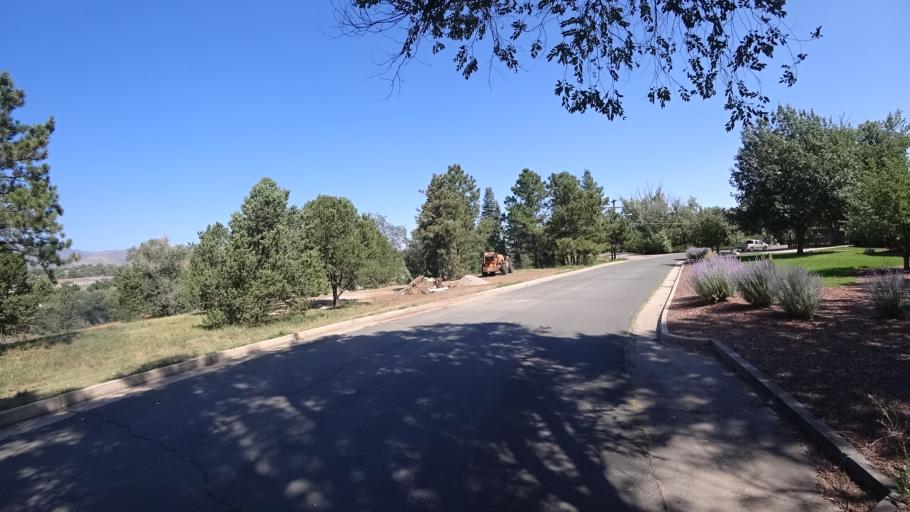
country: US
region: Colorado
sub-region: El Paso County
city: Colorado Springs
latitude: 38.8574
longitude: -104.8308
